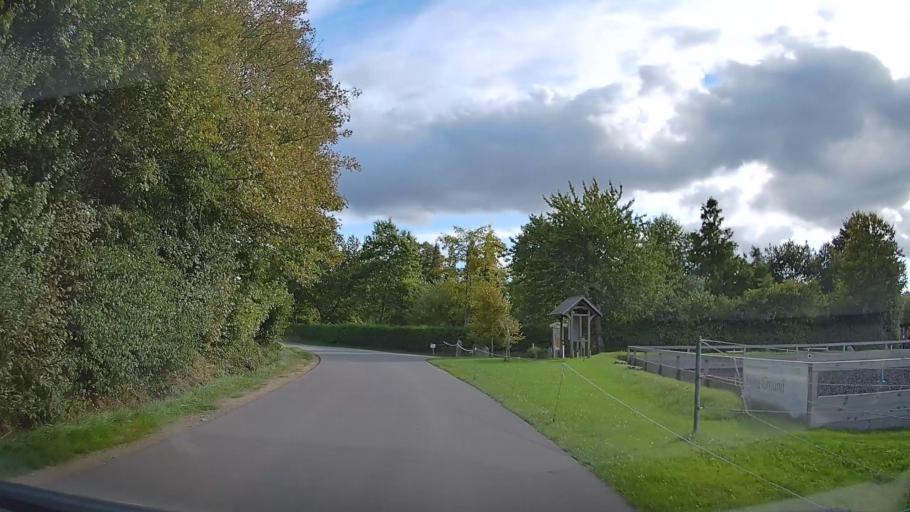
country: DE
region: Schleswig-Holstein
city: Steinberg
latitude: 54.7929
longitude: 9.7782
